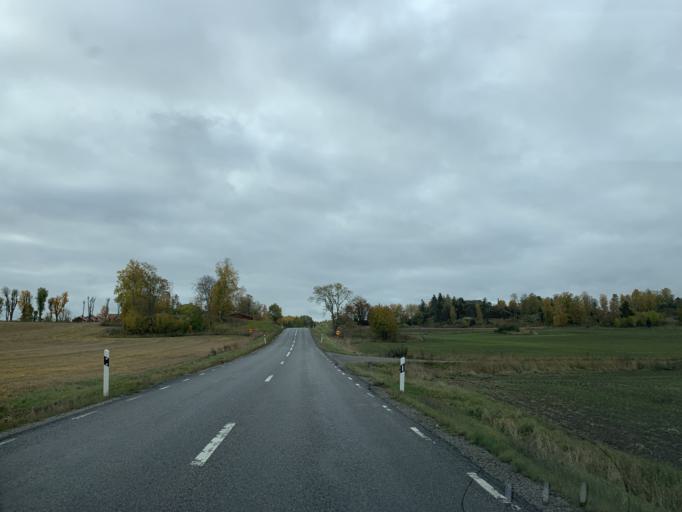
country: SE
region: Stockholm
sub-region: Nynashamns Kommun
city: Osmo
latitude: 59.0374
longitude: 17.8039
